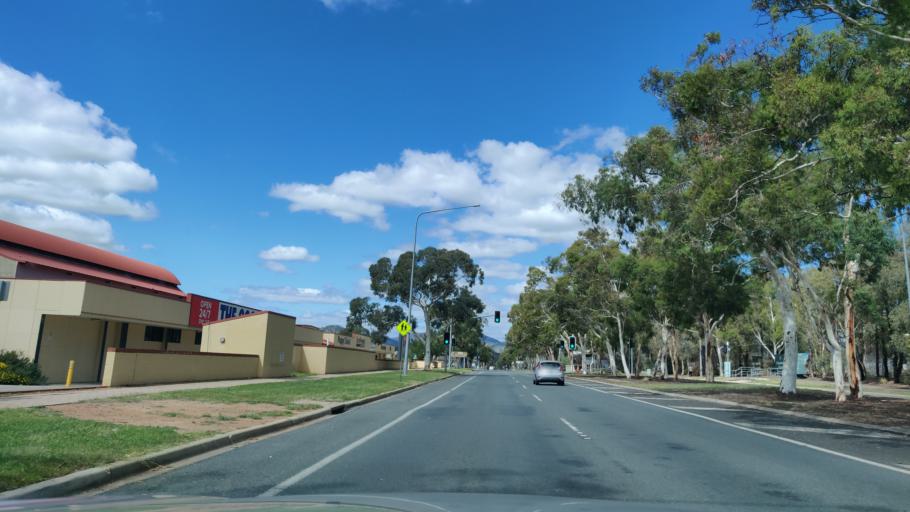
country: AU
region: Australian Capital Territory
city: Macarthur
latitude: -35.4170
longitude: 149.0634
